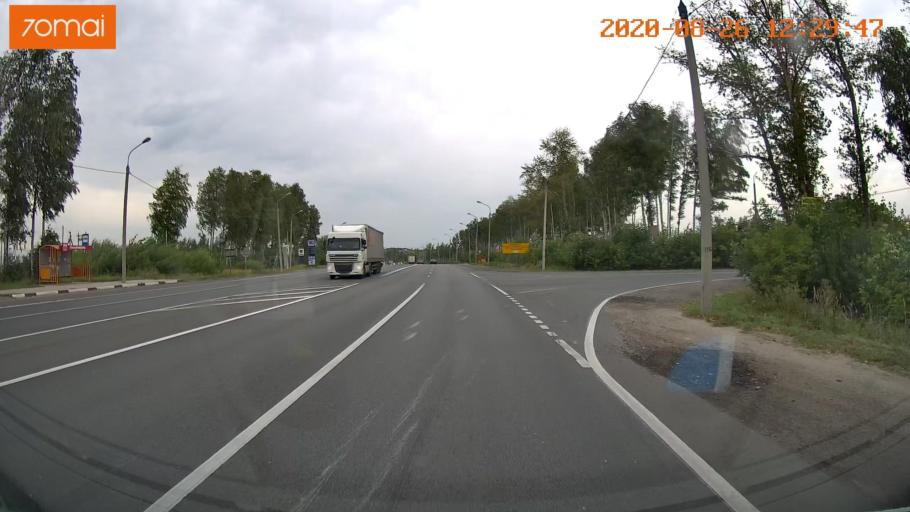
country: RU
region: Rjazan
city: Ryazan'
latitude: 54.5659
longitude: 39.8128
